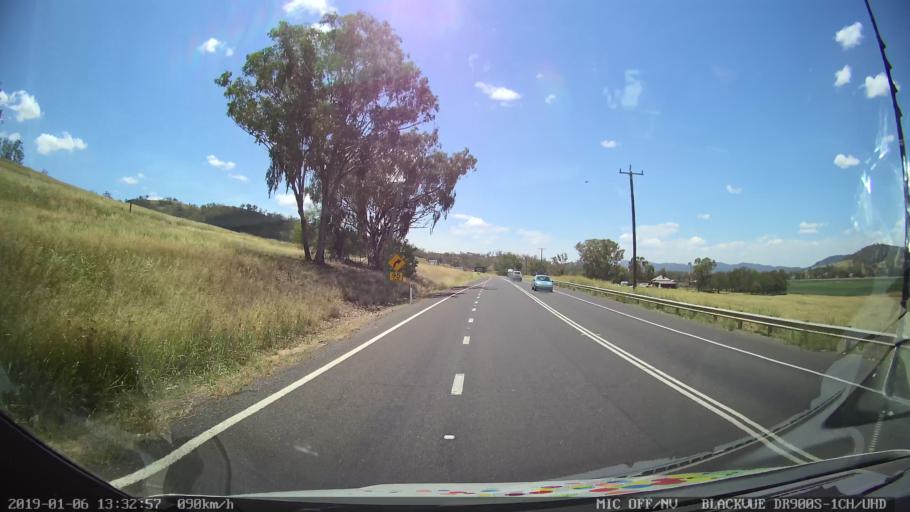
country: AU
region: New South Wales
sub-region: Tamworth Municipality
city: East Tamworth
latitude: -31.1045
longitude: 151.0018
